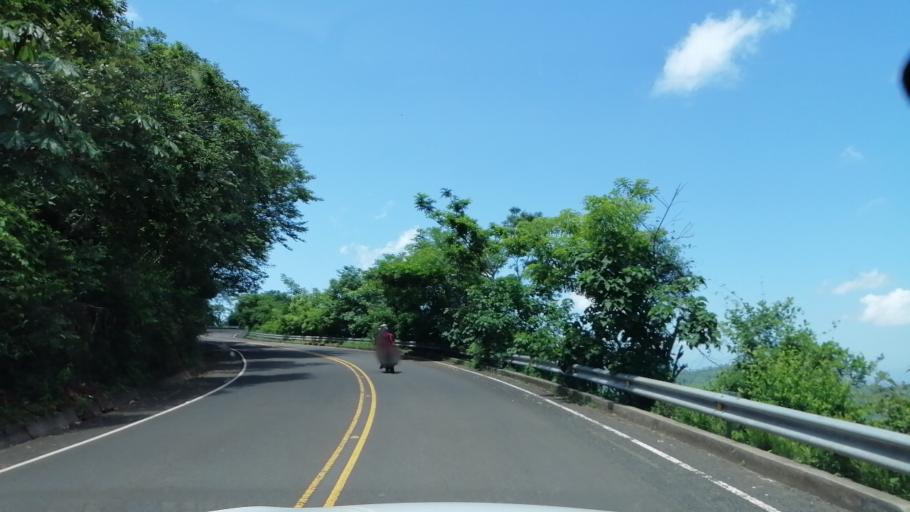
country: SV
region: San Miguel
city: Ciudad Barrios
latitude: 13.7924
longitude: -88.2902
